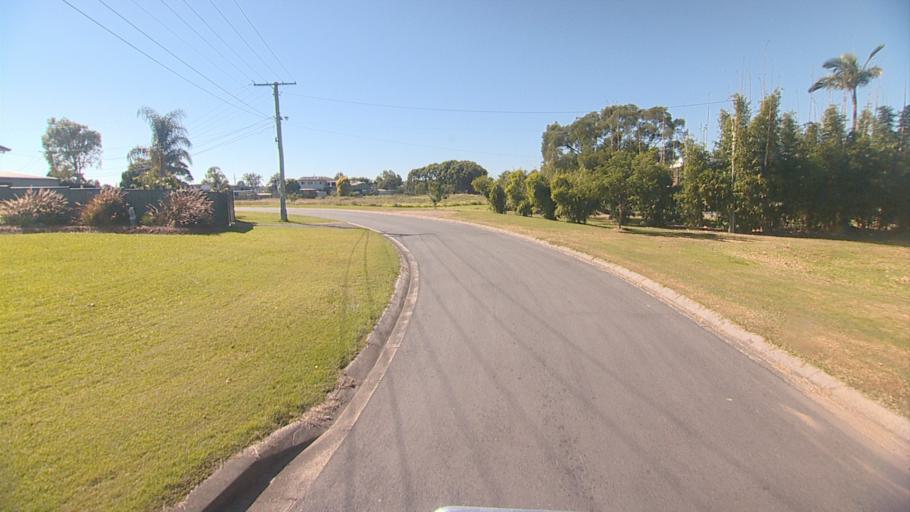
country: AU
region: Queensland
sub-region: Logan
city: Waterford West
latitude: -27.6895
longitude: 153.1415
